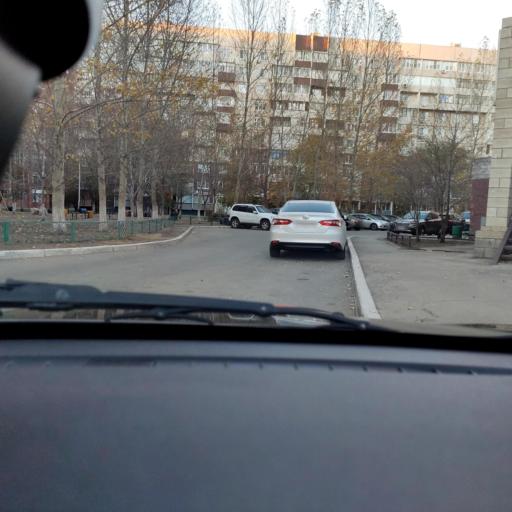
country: RU
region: Samara
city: Tol'yatti
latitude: 53.5453
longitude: 49.3205
